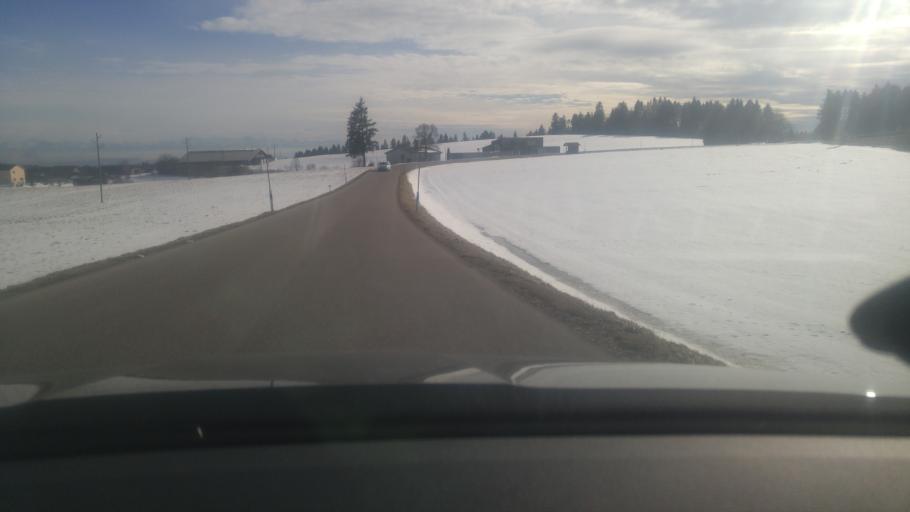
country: DE
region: Baden-Wuerttemberg
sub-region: Freiburg Region
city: Hochenschwand
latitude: 47.7142
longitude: 8.1522
